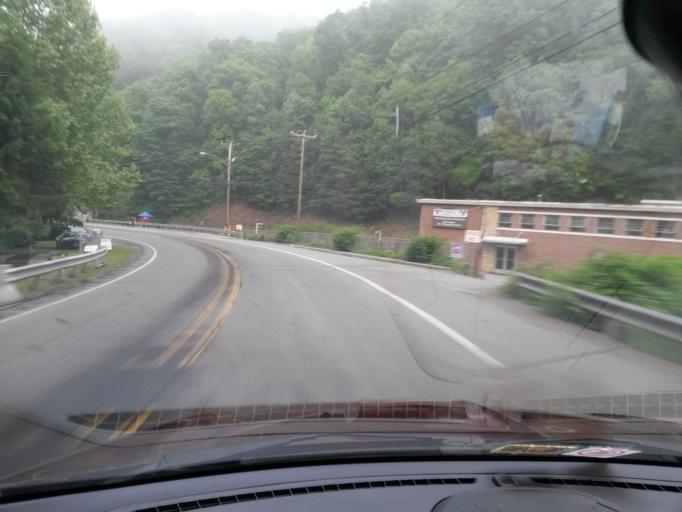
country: US
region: West Virginia
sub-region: McDowell County
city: Welch
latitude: 37.4486
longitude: -81.5636
